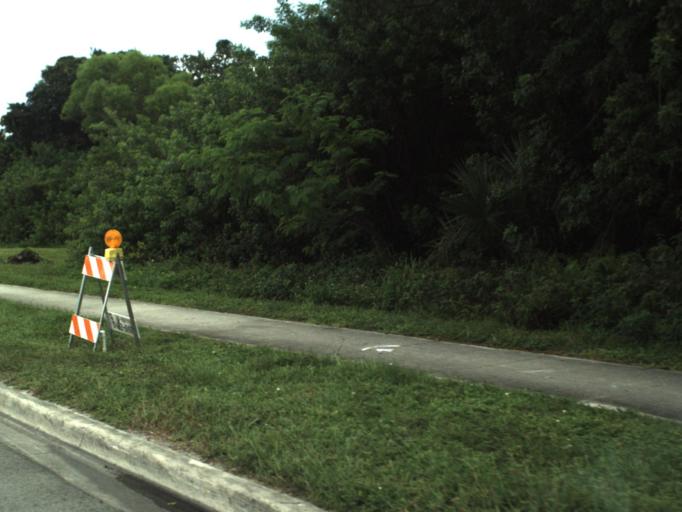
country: US
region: Florida
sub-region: Broward County
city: Margate
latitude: 26.2341
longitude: -80.1927
